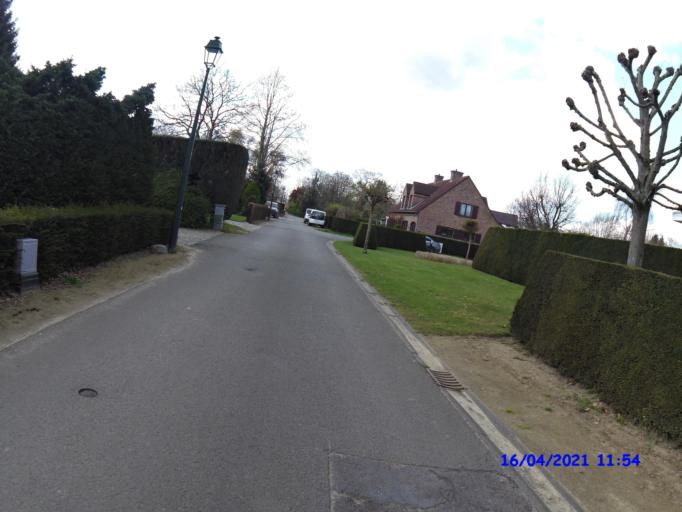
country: BE
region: Flanders
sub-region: Provincie Oost-Vlaanderen
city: Sint-Martens-Latem
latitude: 51.0203
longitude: 3.6488
